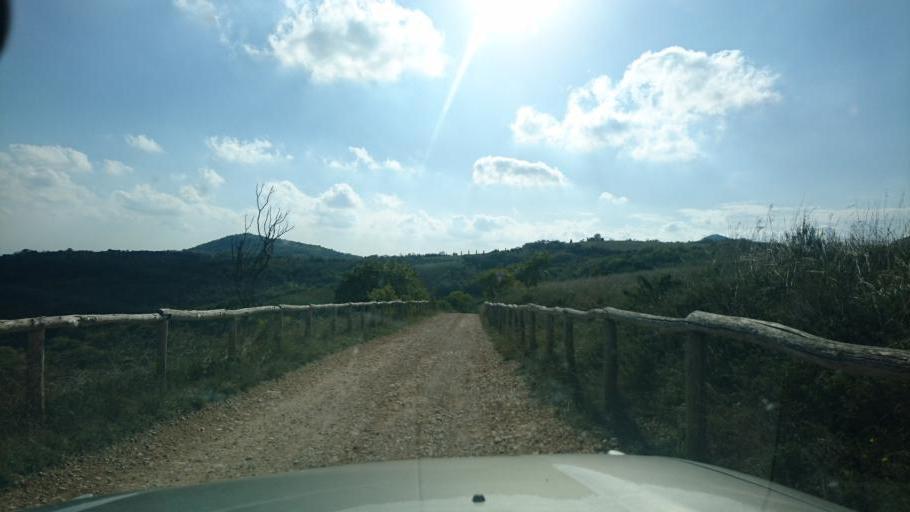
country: IT
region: Veneto
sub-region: Provincia di Padova
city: Arqua Petrarca
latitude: 45.2647
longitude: 11.6989
